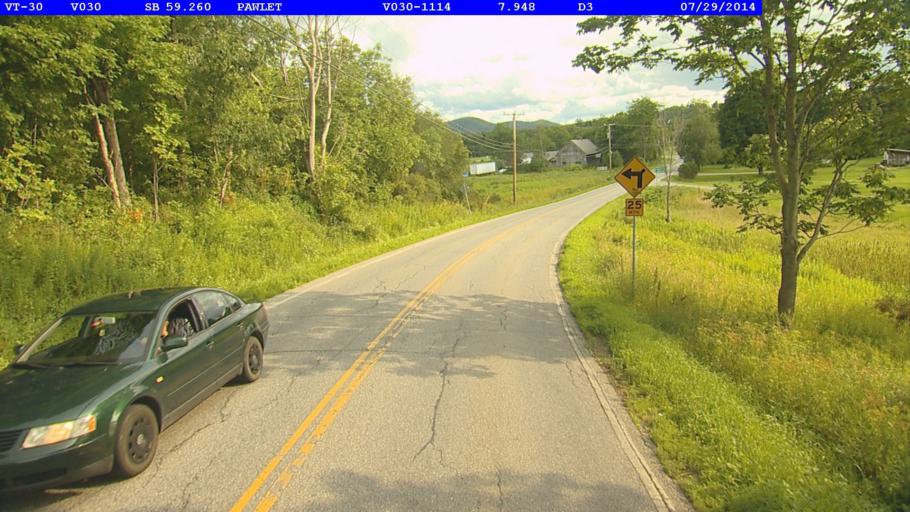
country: US
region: New York
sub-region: Washington County
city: Granville
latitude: 43.4033
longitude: -73.2252
